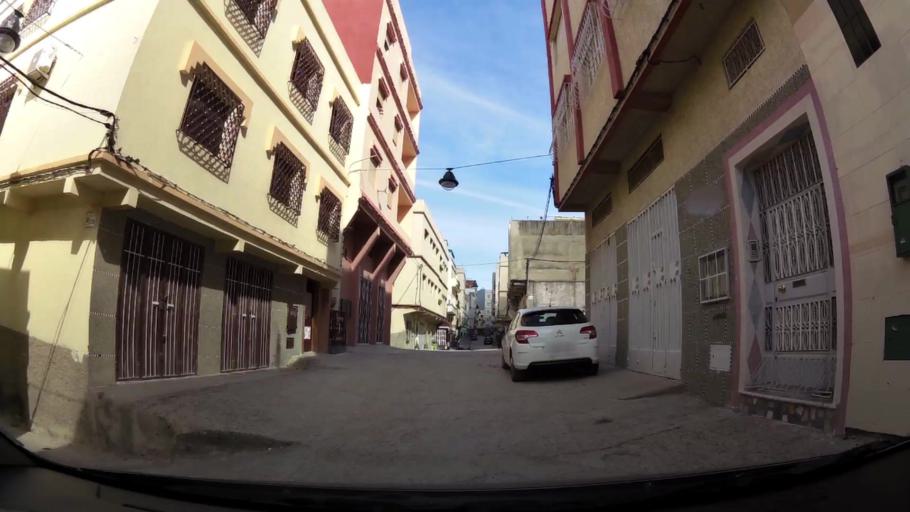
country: MA
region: Tanger-Tetouan
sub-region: Tanger-Assilah
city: Tangier
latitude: 35.7682
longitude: -5.7678
